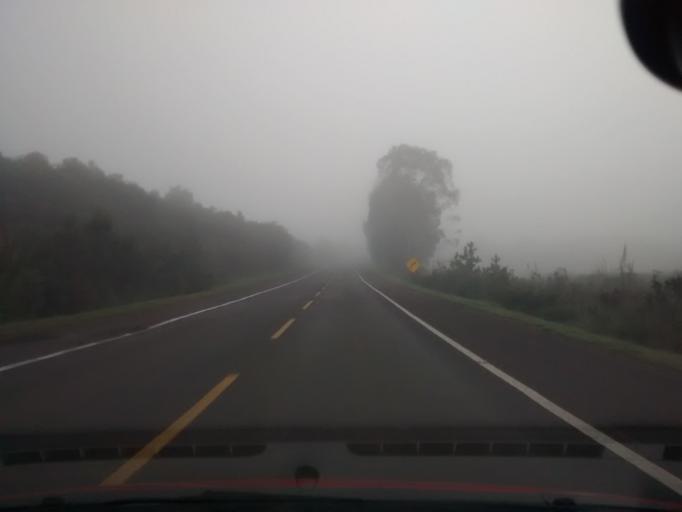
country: BR
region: Rio Grande do Sul
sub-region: Vacaria
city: Vacaria
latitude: -28.3170
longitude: -50.8045
